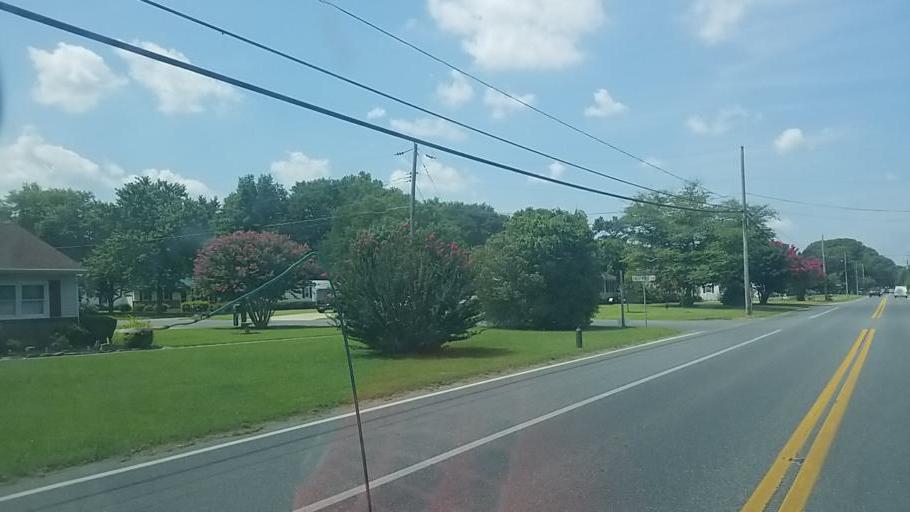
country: US
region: Maryland
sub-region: Wicomico County
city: Salisbury
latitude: 38.3597
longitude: -75.5484
